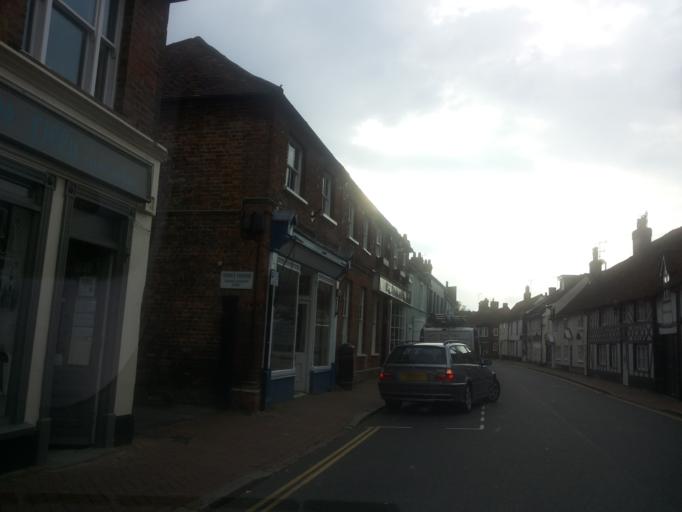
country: GB
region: England
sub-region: Buckinghamshire
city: Great Missenden
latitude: 51.7029
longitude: -0.7068
